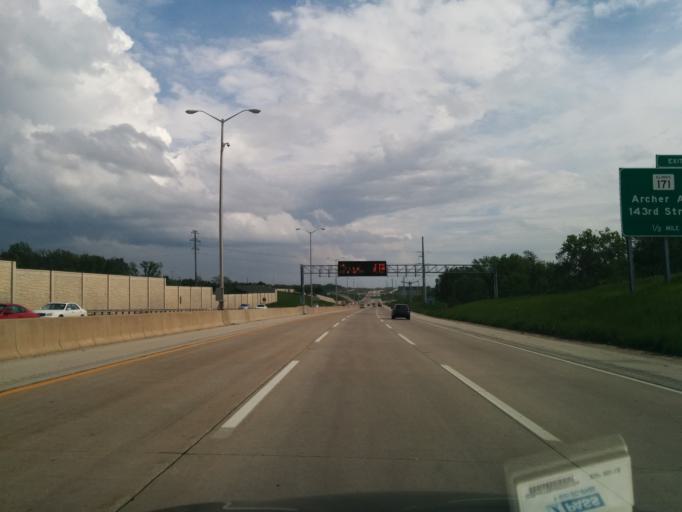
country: US
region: Illinois
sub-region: Cook County
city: Lemont
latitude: 41.6482
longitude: -88.0141
